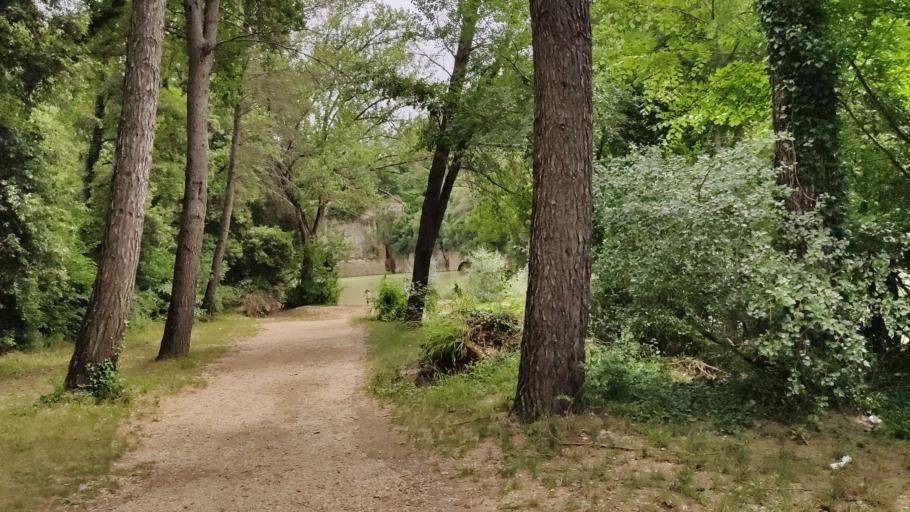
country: IT
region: Umbria
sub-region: Provincia di Terni
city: Amelia
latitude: 42.5628
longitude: 12.4205
